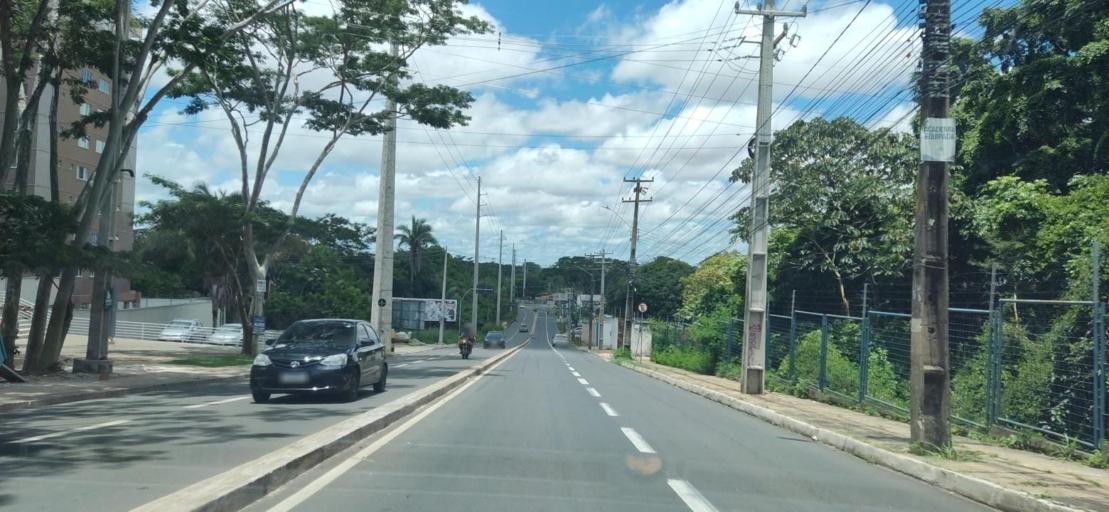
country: BR
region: Piaui
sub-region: Teresina
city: Teresina
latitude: -5.0834
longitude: -42.7658
